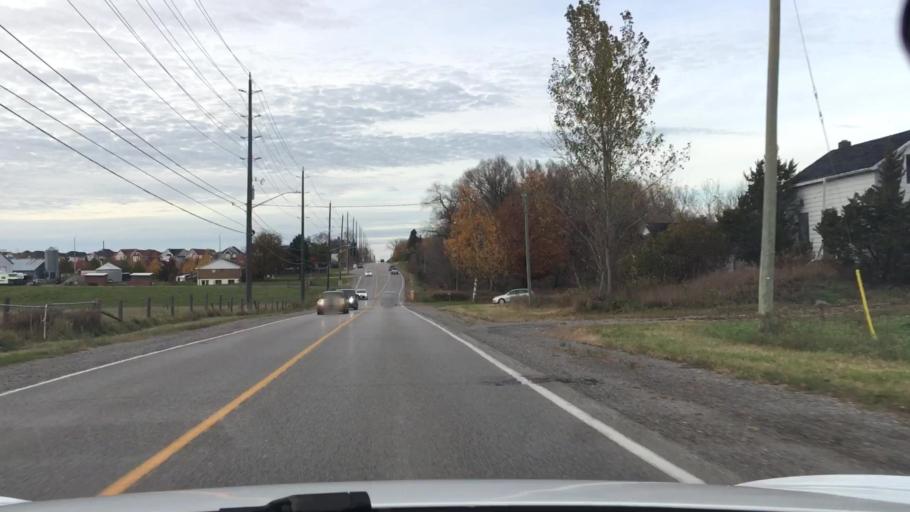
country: CA
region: Ontario
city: Oshawa
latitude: 43.9331
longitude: -78.8250
